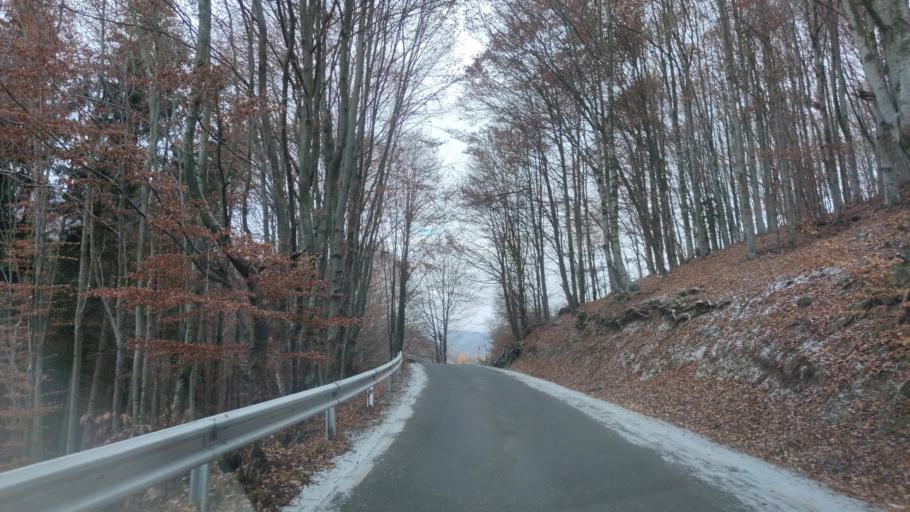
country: RO
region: Harghita
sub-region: Comuna Corund
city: Corund
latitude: 46.4806
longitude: 25.2206
